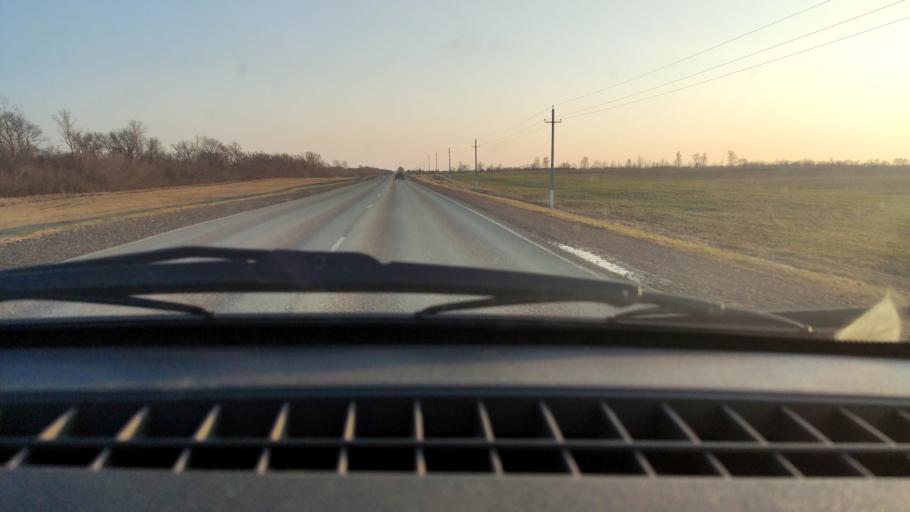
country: RU
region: Bashkortostan
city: Davlekanovo
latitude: 54.3085
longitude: 55.1413
